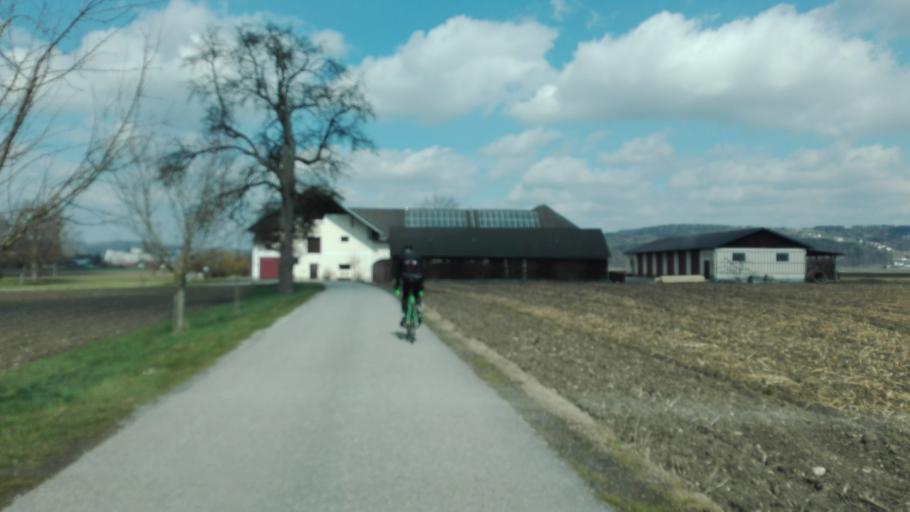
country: AT
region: Upper Austria
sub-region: Politischer Bezirk Urfahr-Umgebung
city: Feldkirchen an der Donau
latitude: 48.3426
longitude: 14.0329
